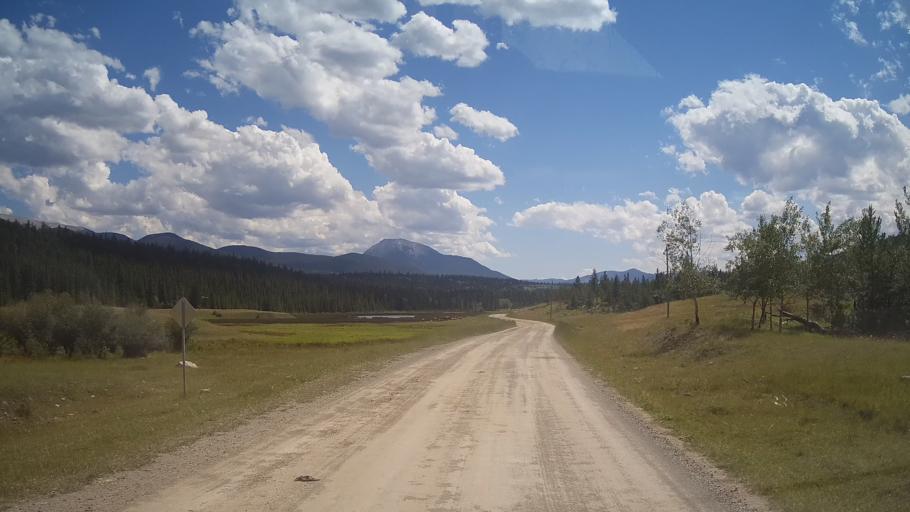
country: CA
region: British Columbia
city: Lillooet
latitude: 51.3010
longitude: -121.9830
